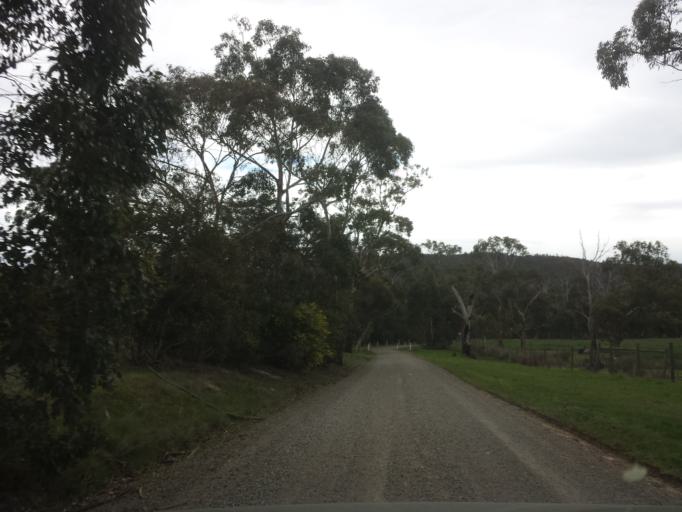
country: AU
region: Victoria
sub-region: Yarra Ranges
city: Yarra Glen
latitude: -37.5829
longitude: 145.3876
